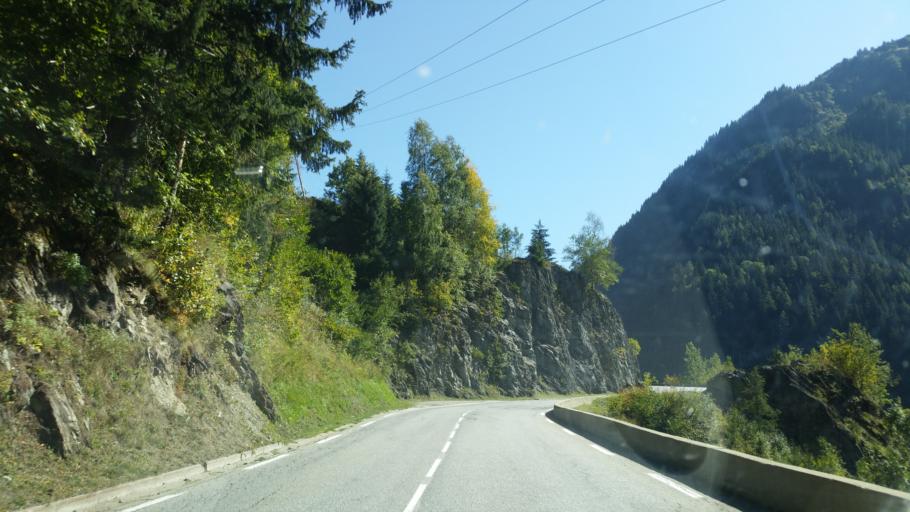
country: FR
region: Rhone-Alpes
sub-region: Departement de la Savoie
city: Tignes
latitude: 45.5681
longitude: 6.8892
